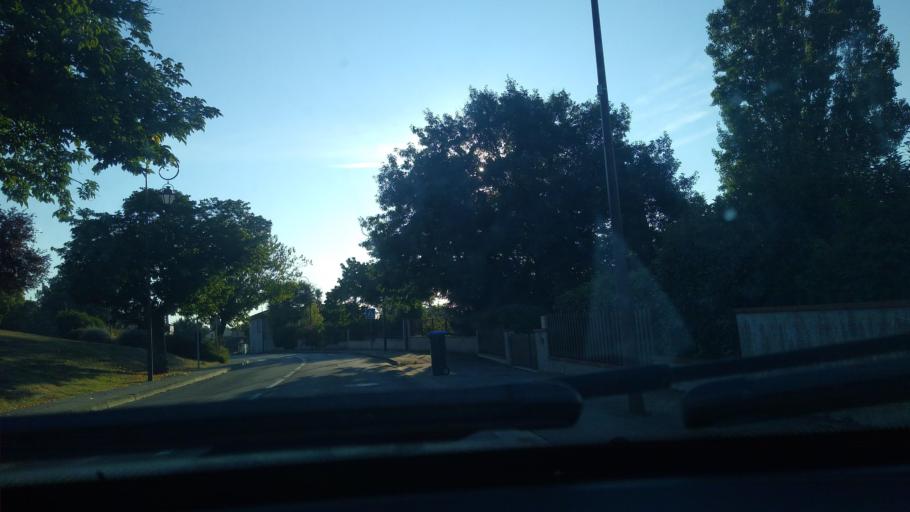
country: FR
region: Midi-Pyrenees
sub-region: Departement de la Haute-Garonne
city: Pibrac
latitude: 43.6171
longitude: 1.2815
